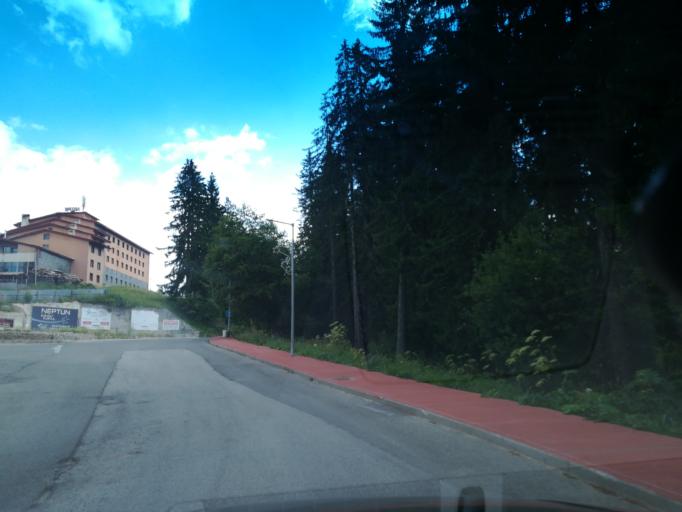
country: BG
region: Smolyan
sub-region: Obshtina Smolyan
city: Smolyan
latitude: 41.6578
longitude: 24.6953
